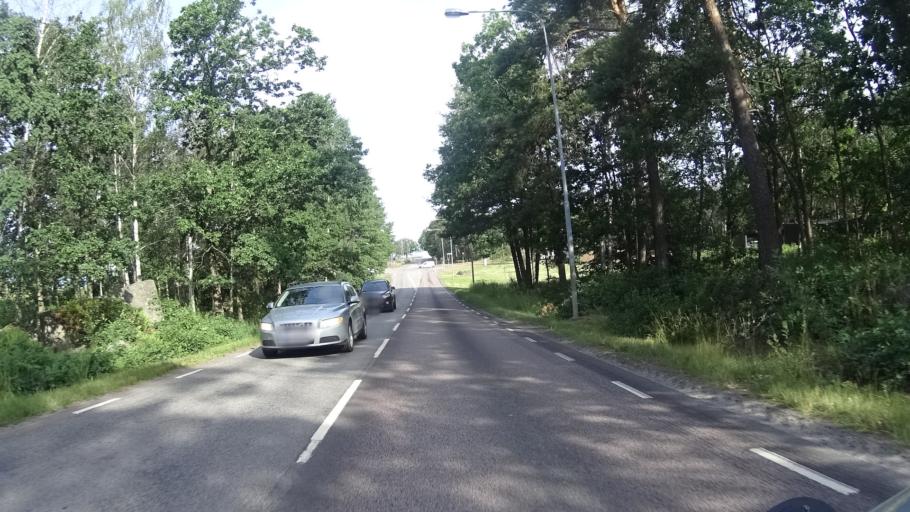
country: SE
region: Kalmar
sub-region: Oskarshamns Kommun
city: Oskarshamn
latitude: 57.2549
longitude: 16.4393
